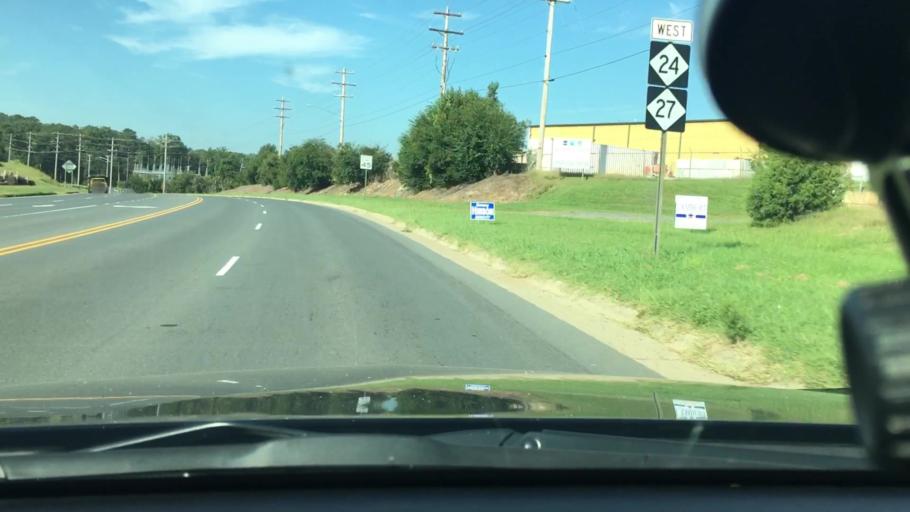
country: US
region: North Carolina
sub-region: Stanly County
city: Albemarle
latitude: 35.3401
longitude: -80.2134
